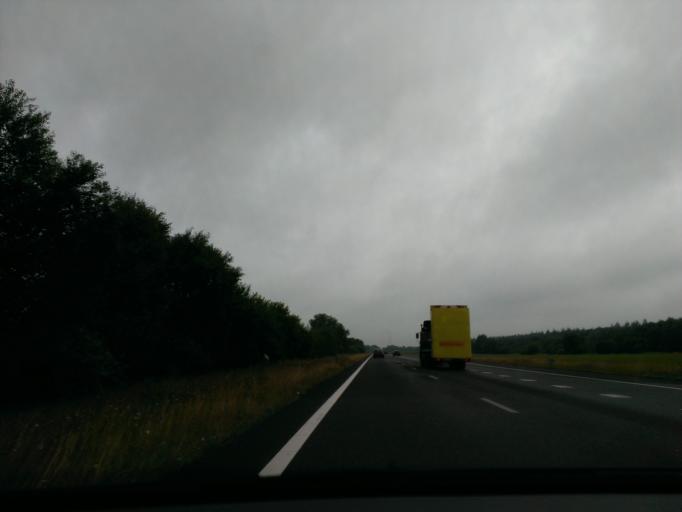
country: NL
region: Drenthe
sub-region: Gemeente Hoogeveen
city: Hoogeveen
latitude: 52.7441
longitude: 6.4624
